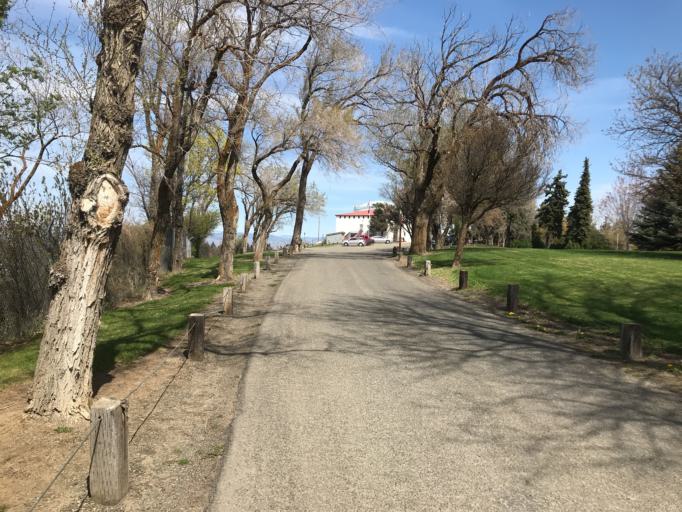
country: US
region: Washington
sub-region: Kittitas County
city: Ellensburg
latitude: 46.9972
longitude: -120.5329
